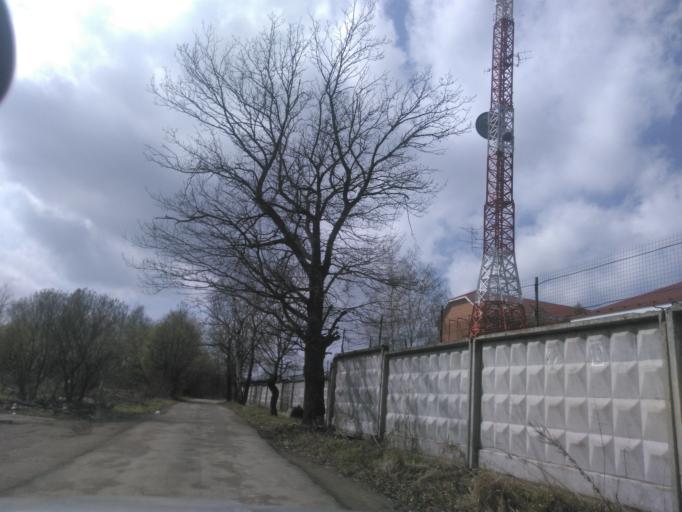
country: RU
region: Moskovskaya
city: Chashnikovo
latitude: 56.0271
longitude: 37.1798
